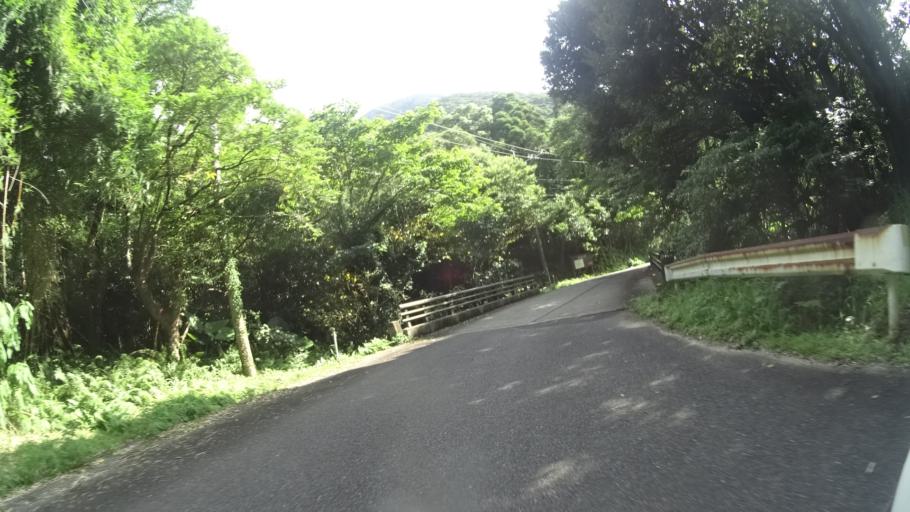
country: JP
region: Kagoshima
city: Nishinoomote
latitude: 30.3897
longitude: 130.3921
